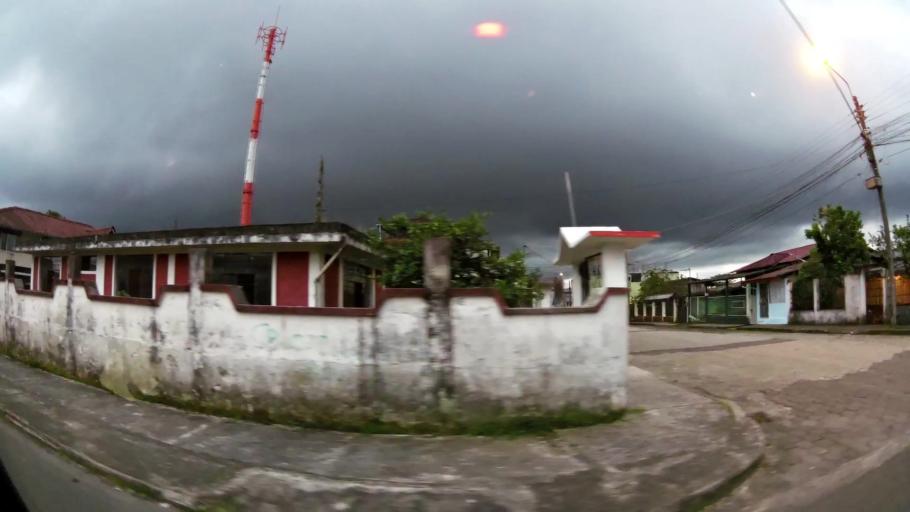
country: EC
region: Pastaza
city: Puyo
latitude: -1.4851
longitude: -78.0085
